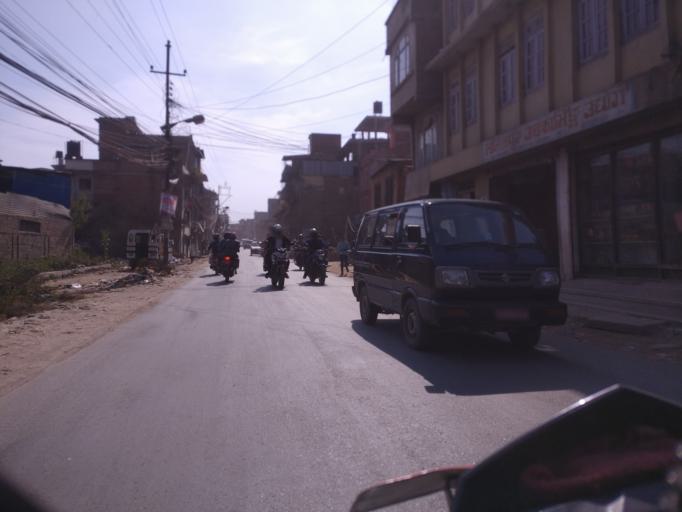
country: NP
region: Central Region
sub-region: Bagmati Zone
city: Patan
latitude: 27.6614
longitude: 85.3238
